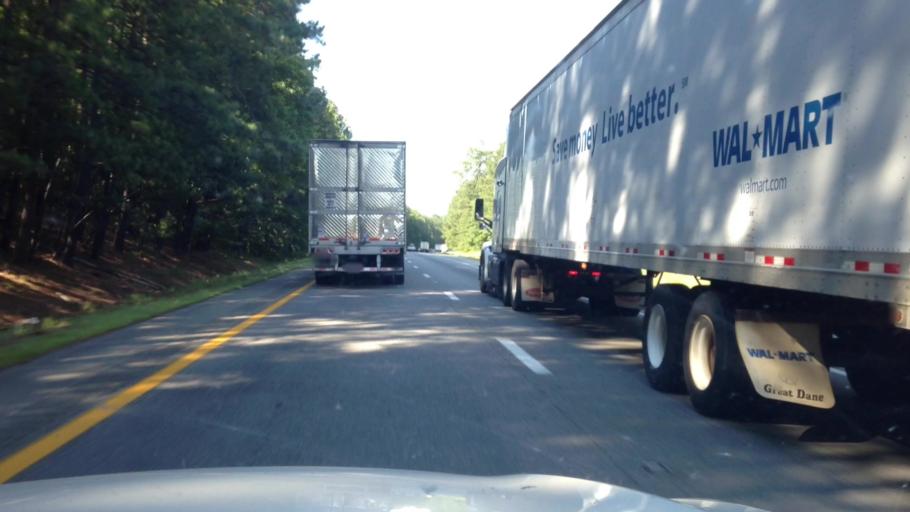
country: US
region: Virginia
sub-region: City of Emporia
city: Emporia
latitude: 36.7466
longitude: -77.5136
